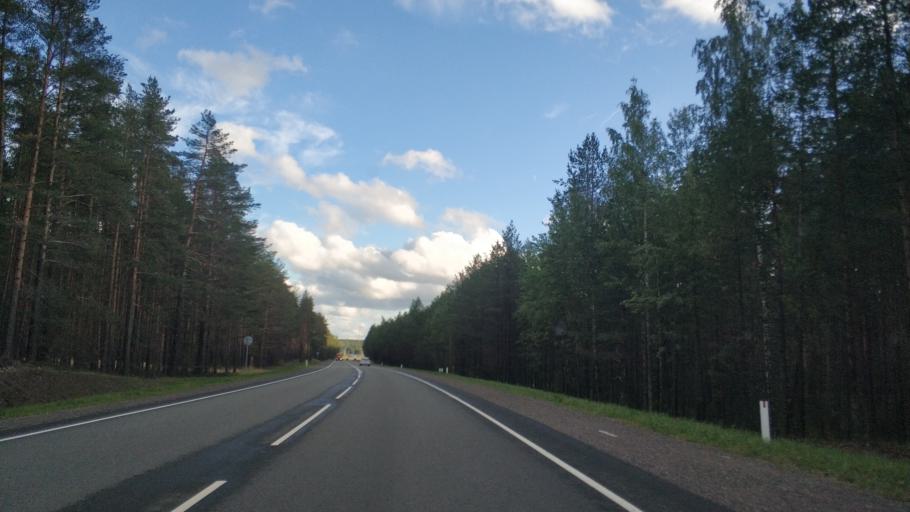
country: RU
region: Leningrad
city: Priozersk
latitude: 60.9848
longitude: 30.1836
